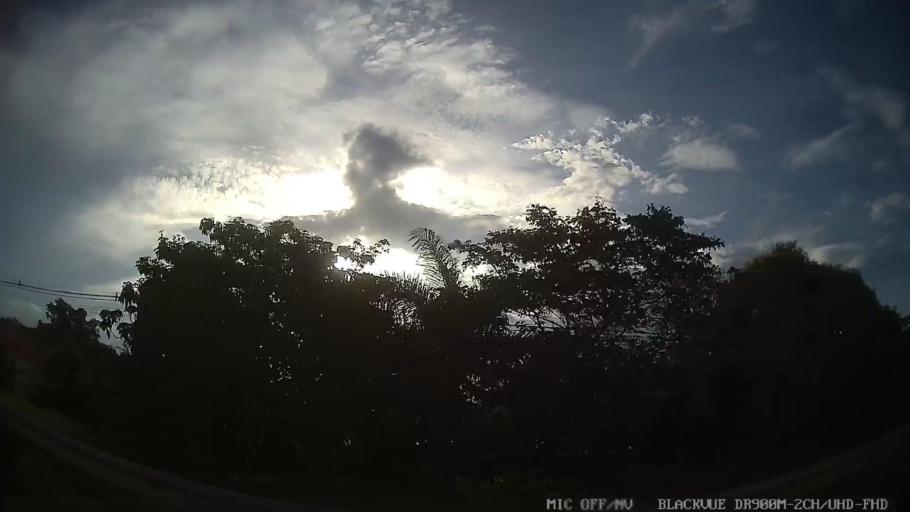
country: BR
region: Sao Paulo
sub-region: Tiete
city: Tiete
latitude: -23.1056
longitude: -47.7247
